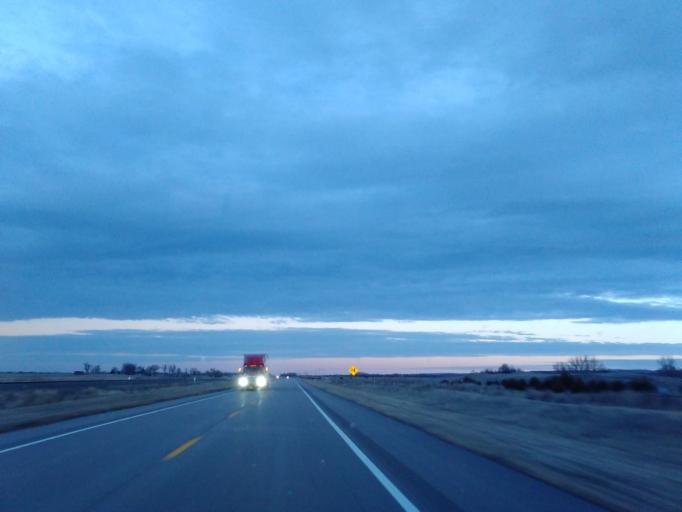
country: US
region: Nebraska
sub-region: Garden County
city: Oshkosh
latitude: 41.3618
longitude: -102.2206
